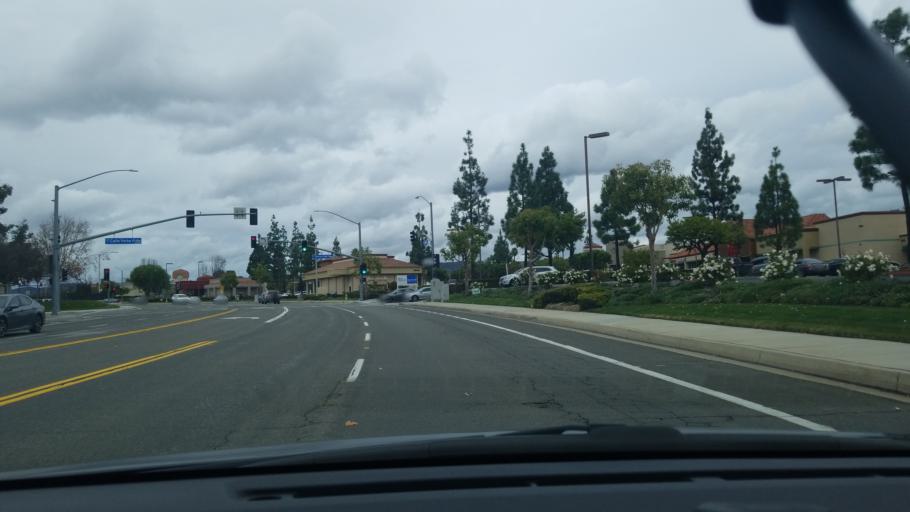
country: US
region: California
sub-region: Riverside County
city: Murrieta Hot Springs
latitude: 33.5691
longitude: -117.1825
